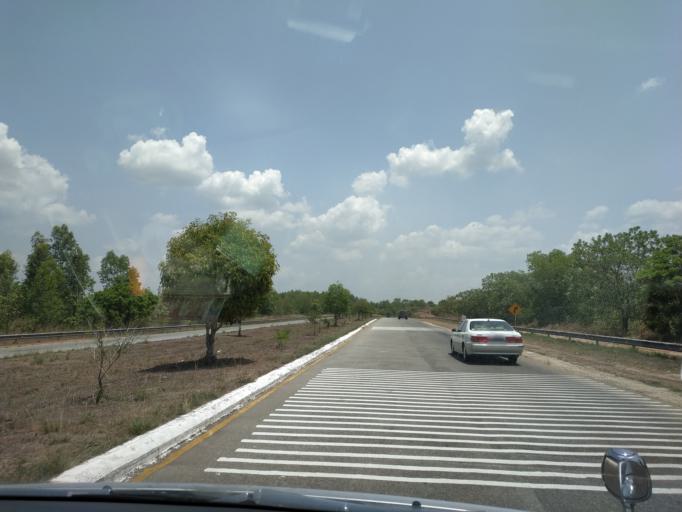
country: MM
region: Bago
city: Thanatpin
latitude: 17.2089
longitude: 96.1930
